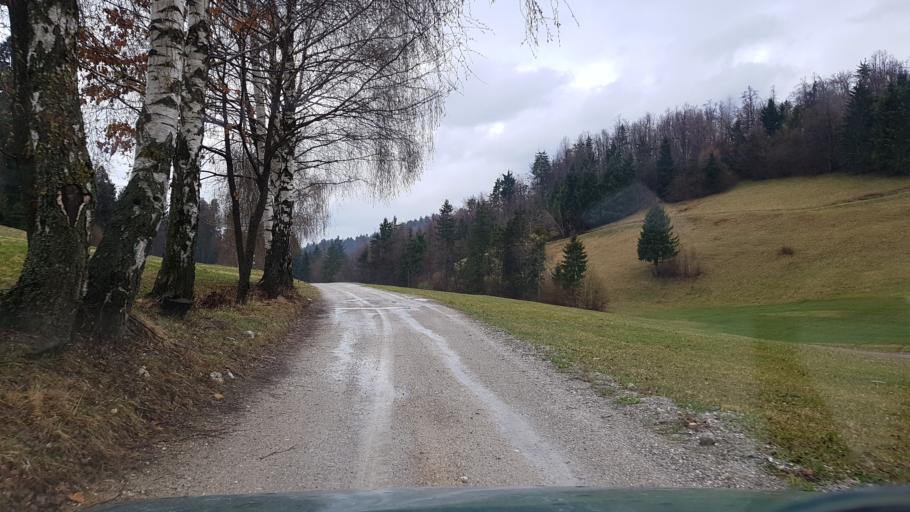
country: SI
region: Tolmin
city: Tolmin
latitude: 46.1388
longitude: 13.8443
